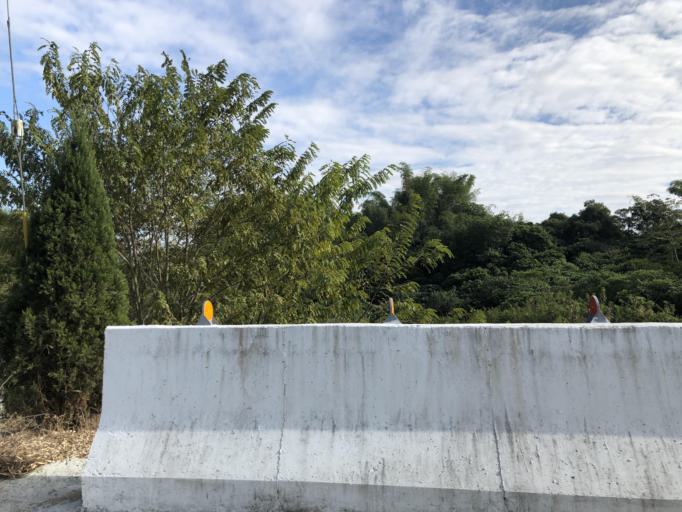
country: TW
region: Taiwan
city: Yujing
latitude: 23.0388
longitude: 120.3967
